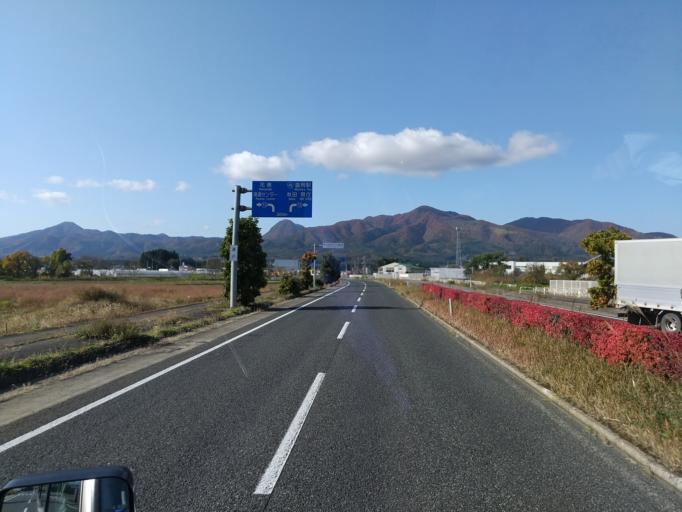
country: JP
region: Iwate
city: Morioka-shi
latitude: 39.6527
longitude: 141.1177
